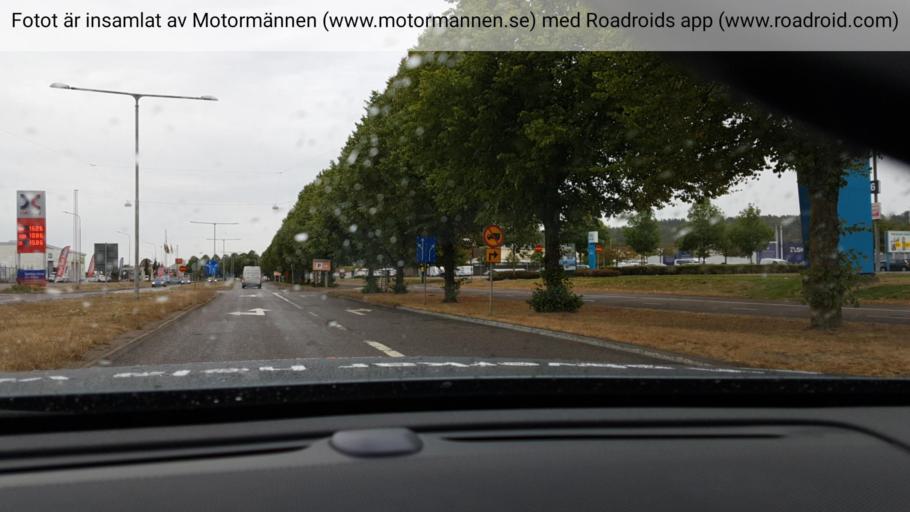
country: SE
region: Vaestra Goetaland
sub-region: Goteborg
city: Hammarkullen
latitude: 57.7701
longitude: 11.9978
